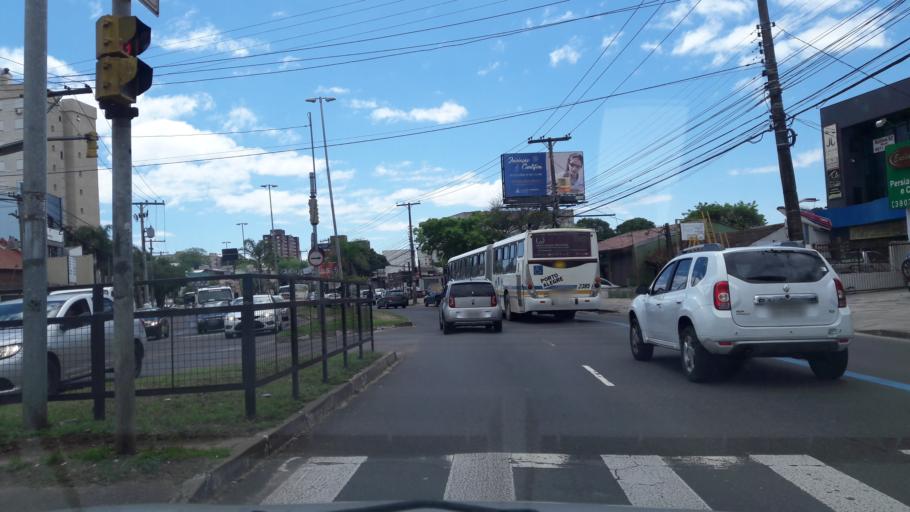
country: BR
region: Rio Grande do Sul
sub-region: Porto Alegre
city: Porto Alegre
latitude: -30.1077
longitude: -51.2274
